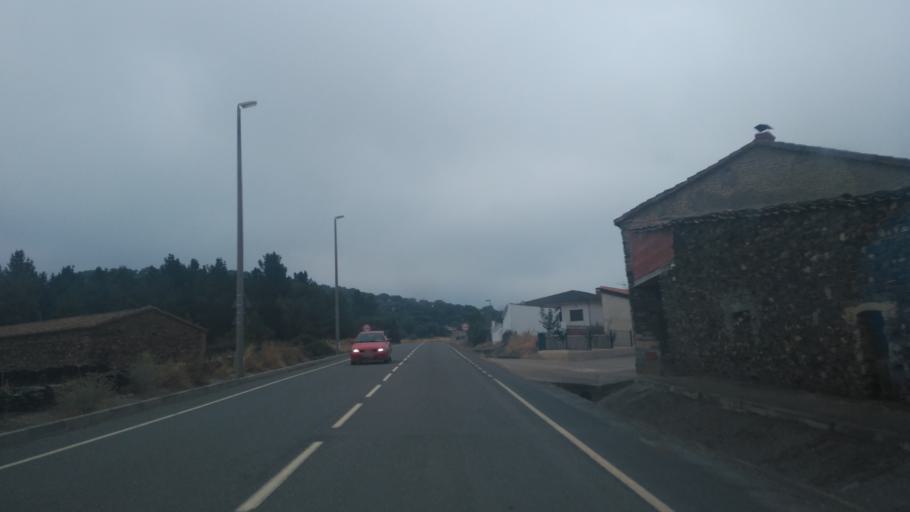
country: ES
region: Castille and Leon
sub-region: Provincia de Salamanca
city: Aldeanueva de la Sierra
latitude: 40.6149
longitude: -6.0983
